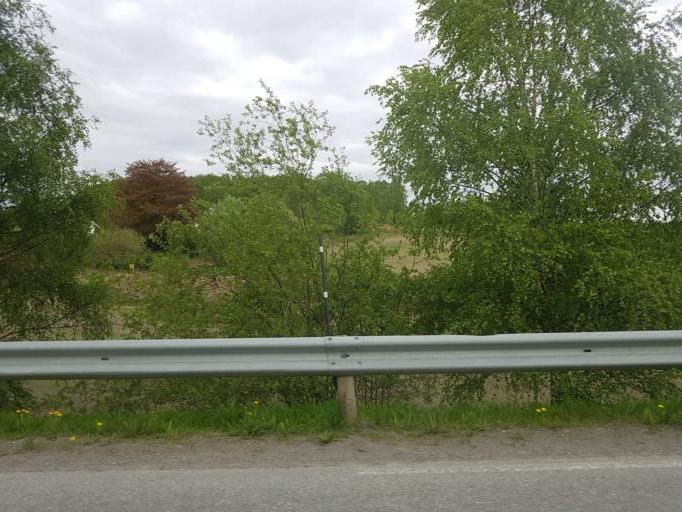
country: NO
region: Nord-Trondelag
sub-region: Levanger
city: Levanger
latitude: 63.7232
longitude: 11.2575
